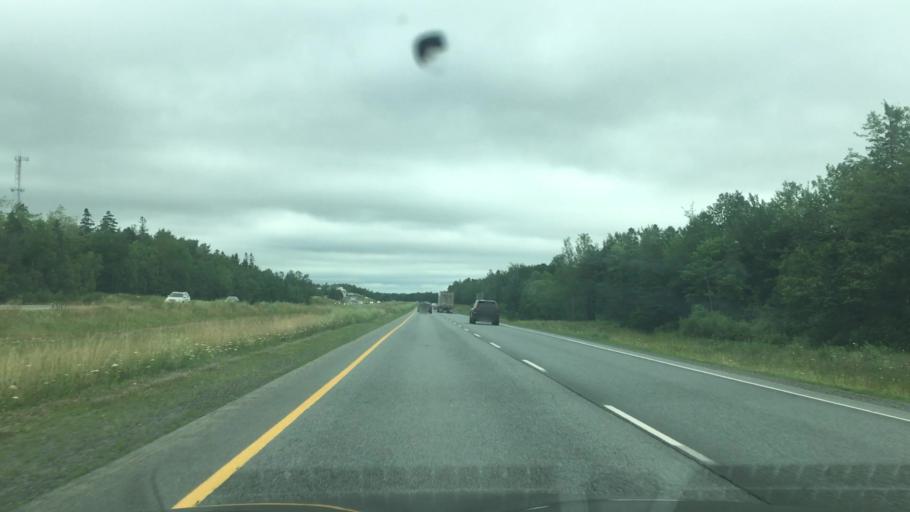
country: CA
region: Nova Scotia
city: Cole Harbour
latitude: 44.9647
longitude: -63.5248
